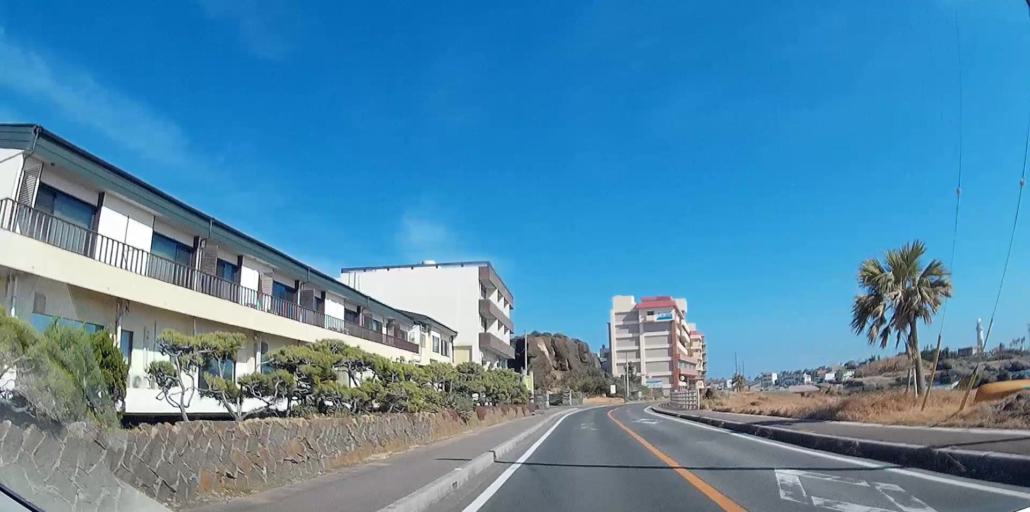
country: JP
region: Chiba
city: Tateyama
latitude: 34.9038
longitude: 139.8839
